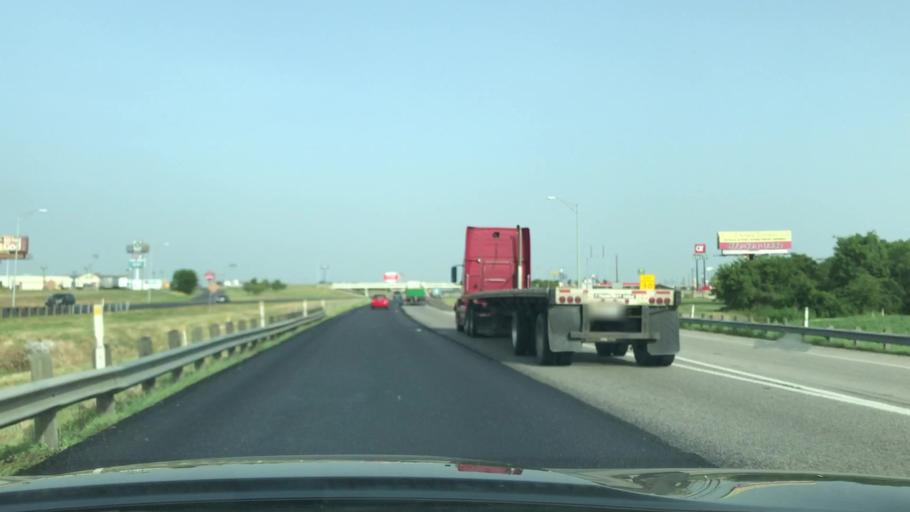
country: US
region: Texas
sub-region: Kaufman County
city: Terrell
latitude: 32.6998
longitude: -96.2701
